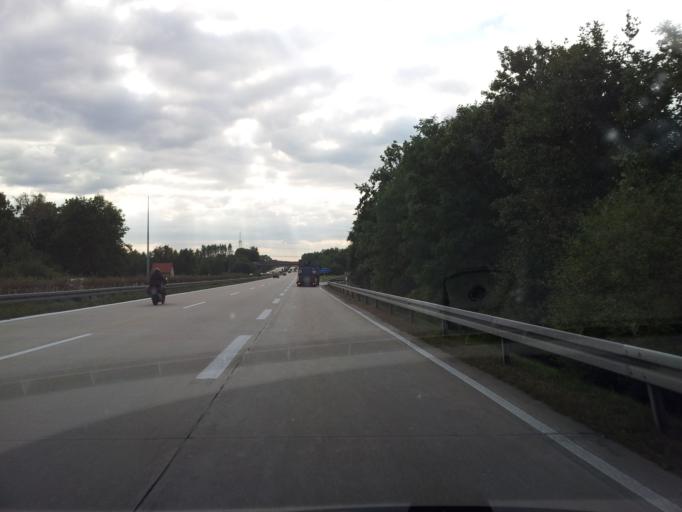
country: DE
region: Brandenburg
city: Schwarzheide
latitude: 51.4707
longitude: 13.8653
